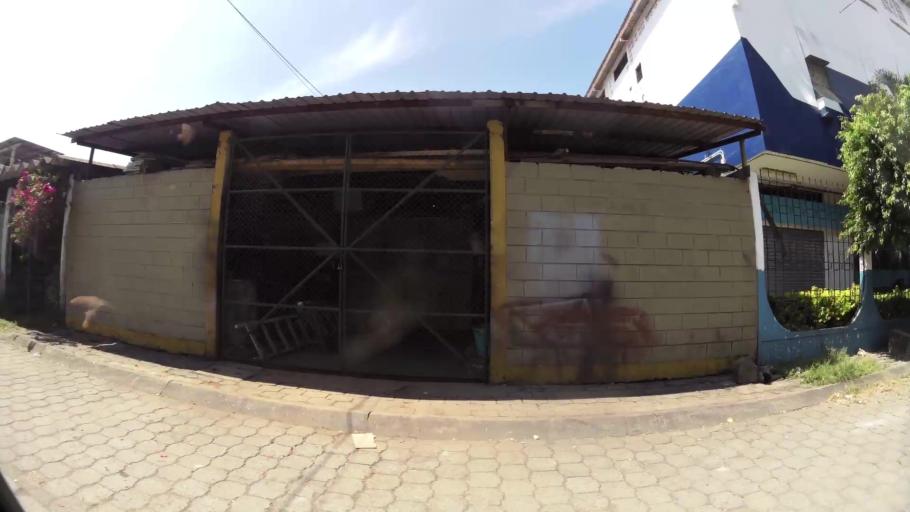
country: EC
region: Guayas
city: Eloy Alfaro
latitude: -2.1121
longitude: -79.9035
